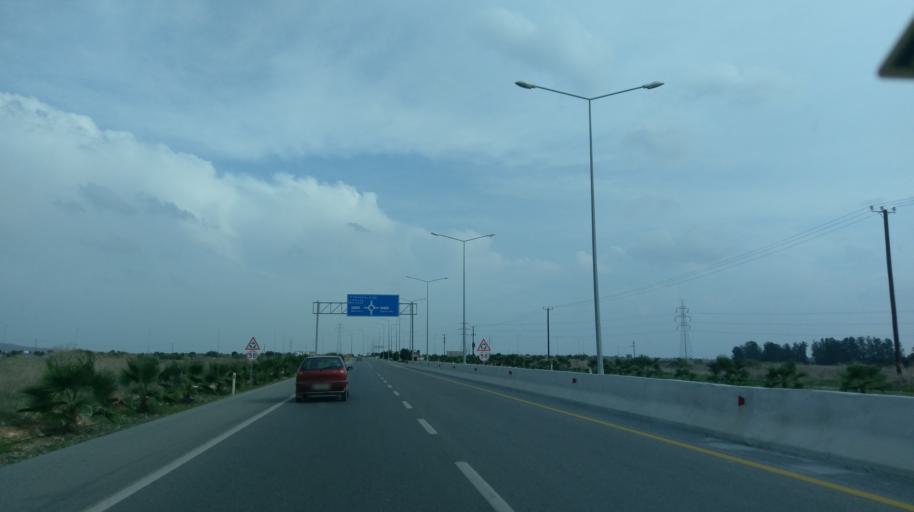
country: CY
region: Lefkosia
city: Astromeritis
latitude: 35.1961
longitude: 33.0610
